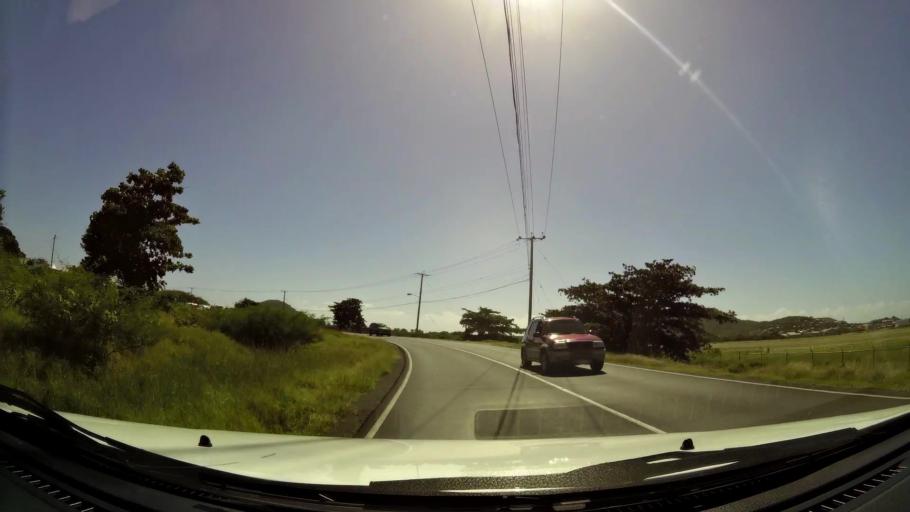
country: LC
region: Vieux-Fort
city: Vieux Fort
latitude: 13.7362
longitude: -60.9452
